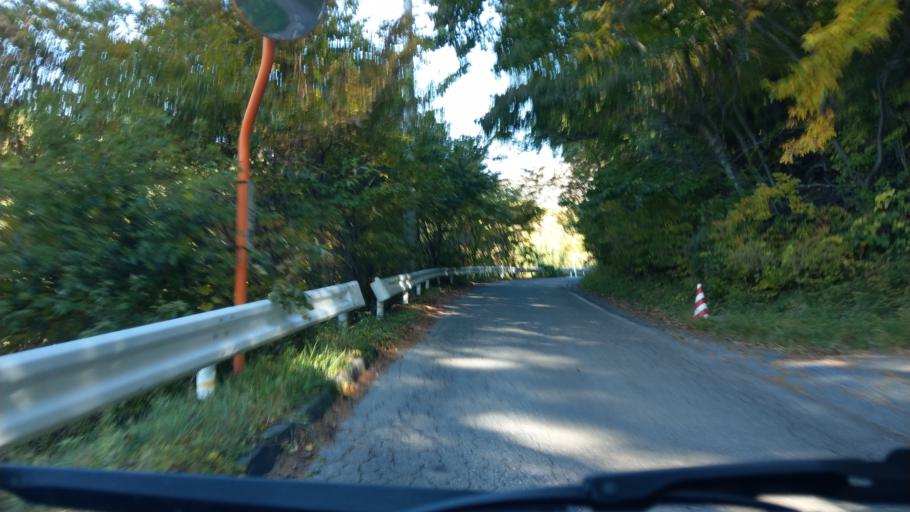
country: JP
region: Nagano
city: Komoro
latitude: 36.3580
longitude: 138.4433
